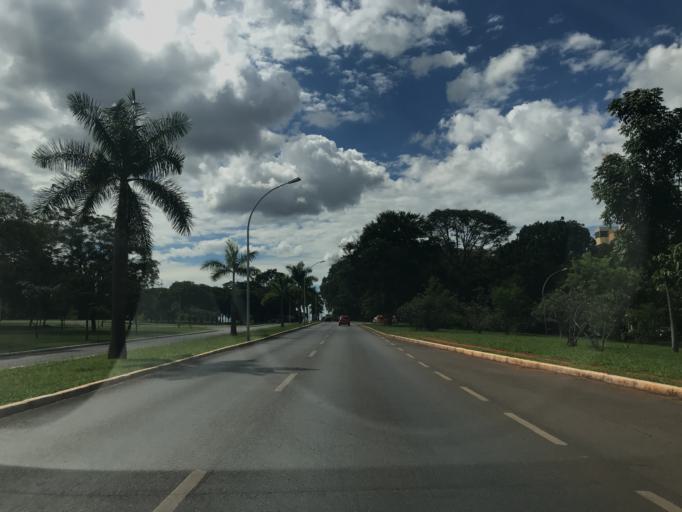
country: BR
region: Federal District
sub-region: Brasilia
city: Brasilia
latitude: -15.7744
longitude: -47.8804
